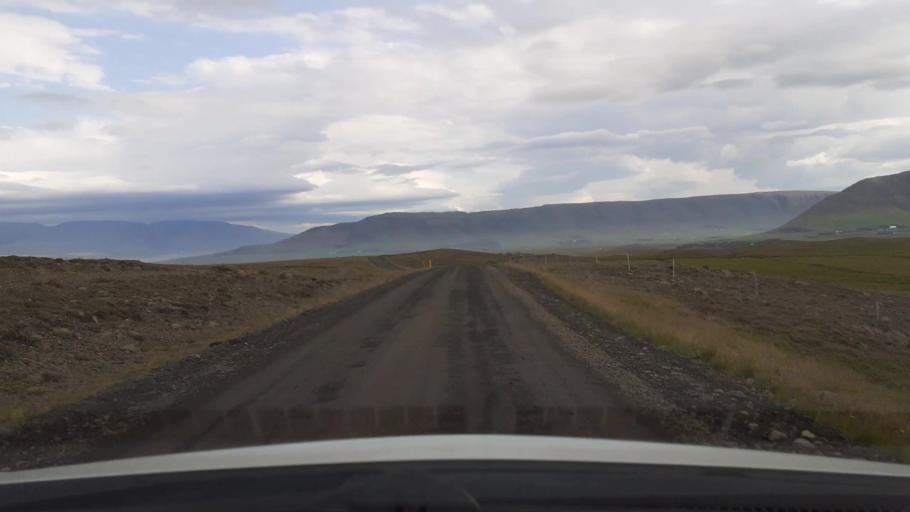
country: IS
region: Capital Region
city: Mosfellsbaer
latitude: 64.3029
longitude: -21.6592
